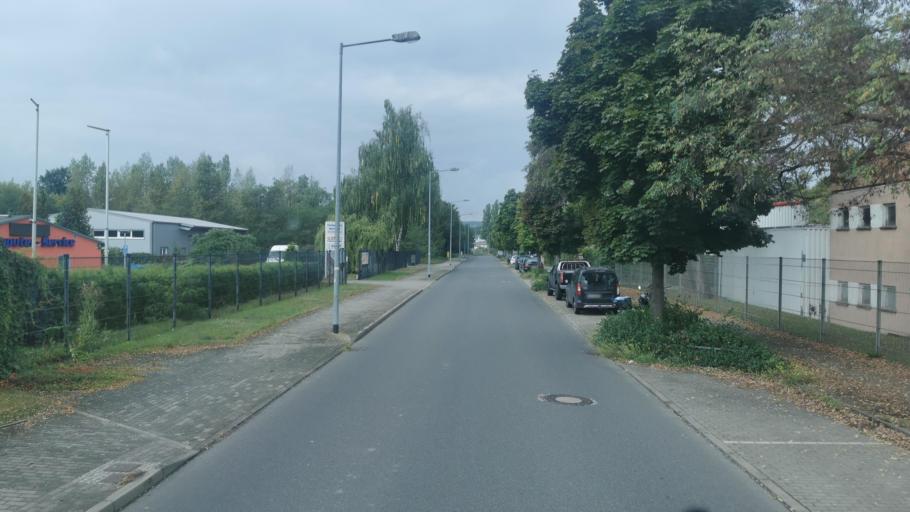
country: DE
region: Brandenburg
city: Eisenhuettenstadt
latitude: 52.1573
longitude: 14.6269
